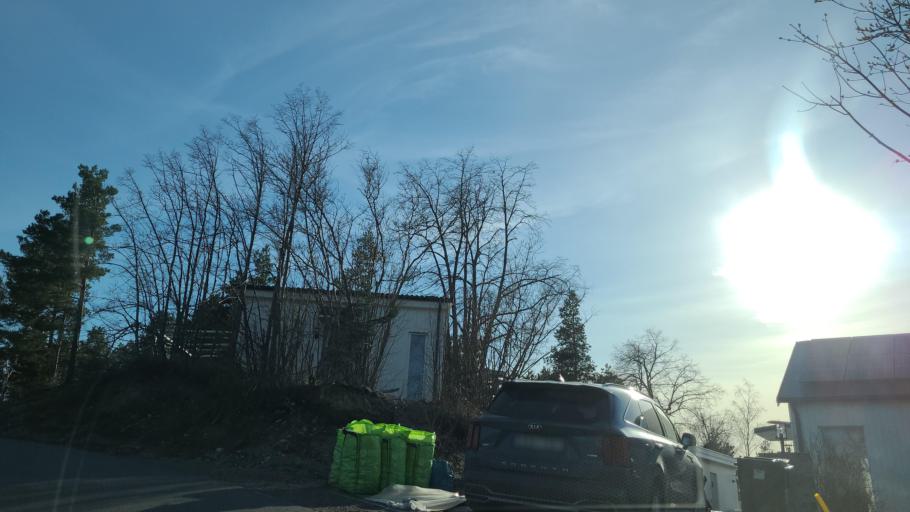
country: SE
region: Stockholm
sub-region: Ekero Kommun
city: Ekeroe
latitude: 59.2641
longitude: 17.7784
